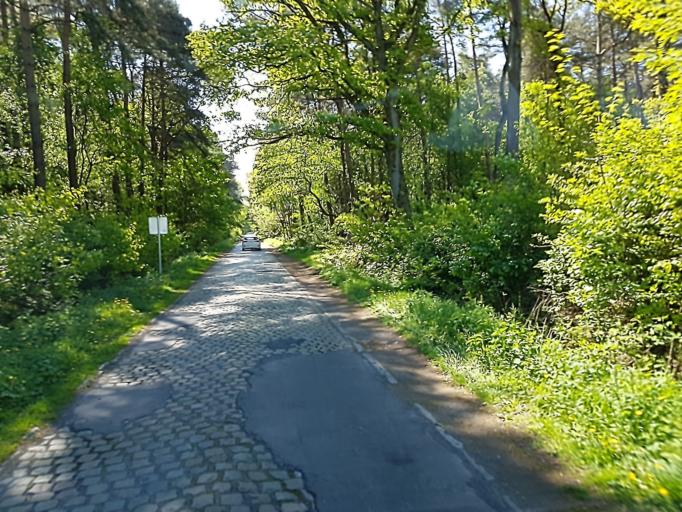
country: BE
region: Wallonia
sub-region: Province du Hainaut
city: Jurbise
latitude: 50.5057
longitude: 3.9058
